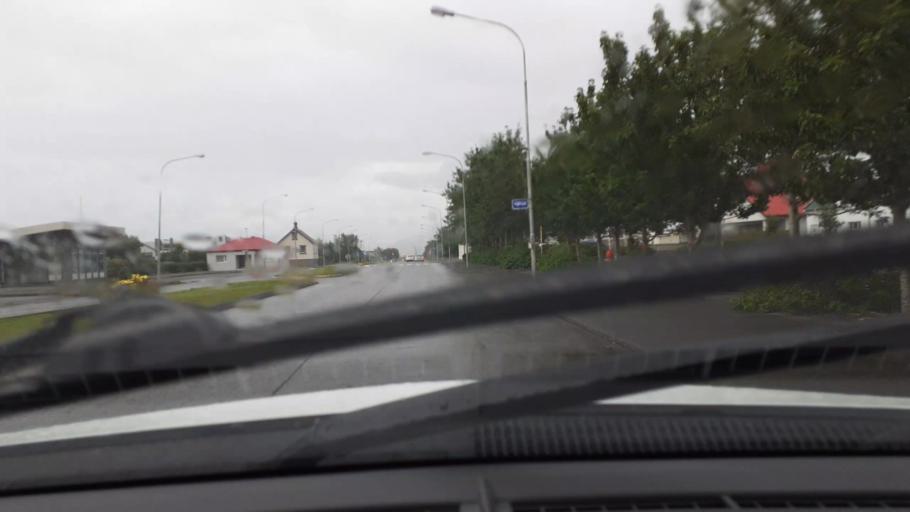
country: IS
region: West
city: Akranes
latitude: 64.3199
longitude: -22.0780
